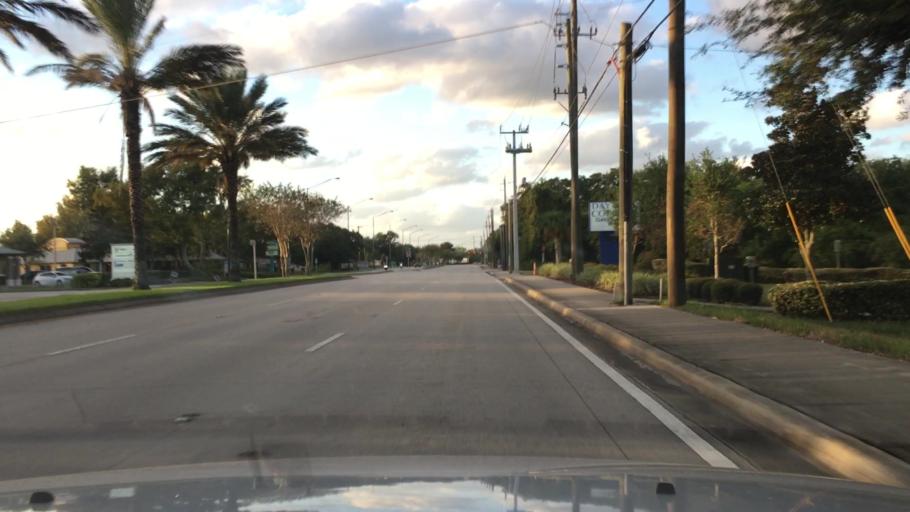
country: US
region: Florida
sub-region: Volusia County
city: Ormond Beach
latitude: 29.2698
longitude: -81.0804
